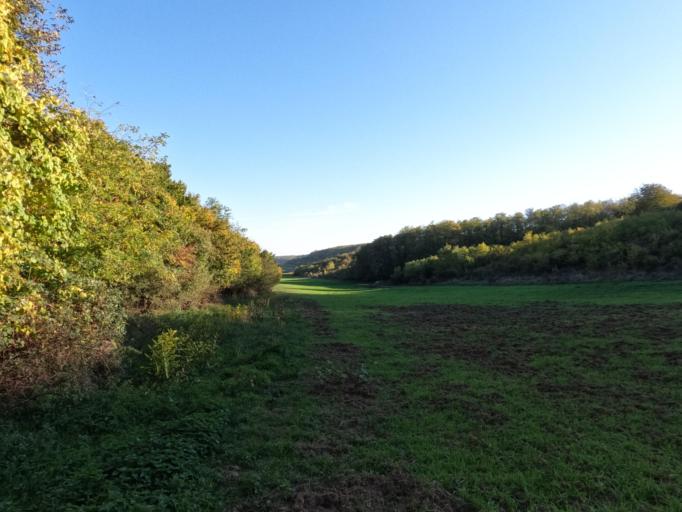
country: HU
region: Tolna
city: Szekszard
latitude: 46.3078
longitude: 18.6534
